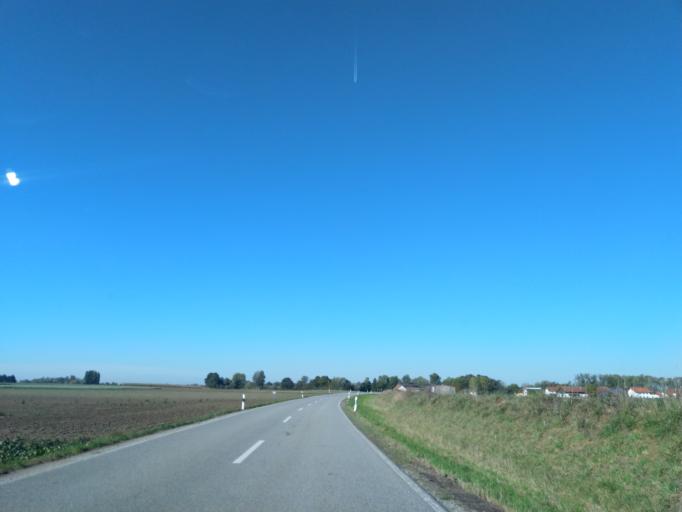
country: DE
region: Bavaria
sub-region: Lower Bavaria
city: Offenberg
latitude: 48.8223
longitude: 12.8711
